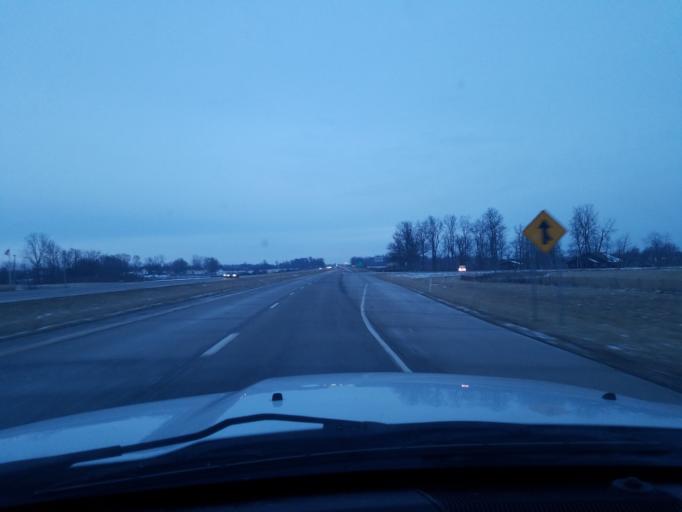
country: US
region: Indiana
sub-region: Delaware County
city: Muncie
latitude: 40.2089
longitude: -85.3362
